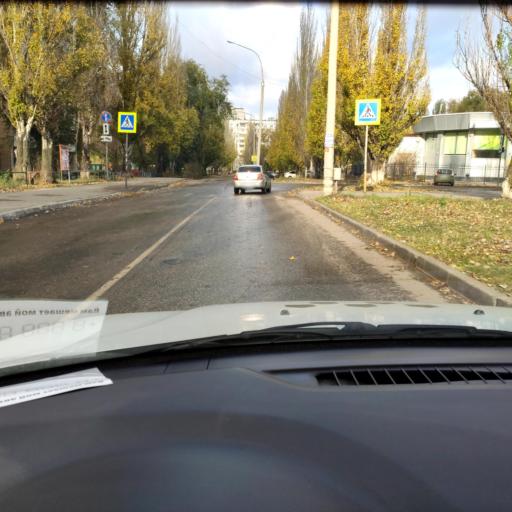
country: RU
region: Samara
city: Tol'yatti
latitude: 53.5341
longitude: 49.2672
